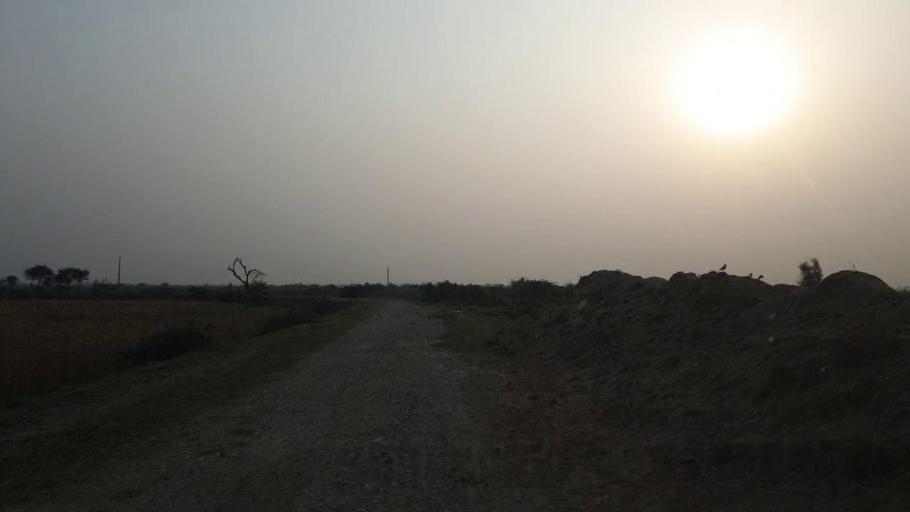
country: PK
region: Sindh
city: Mirpur Batoro
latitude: 24.6628
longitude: 68.3754
